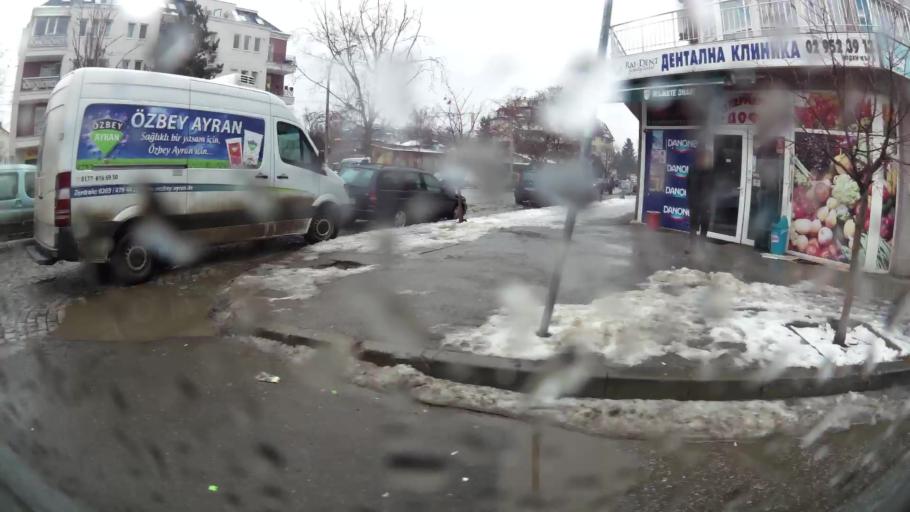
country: BG
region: Sofia-Capital
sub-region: Stolichna Obshtina
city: Sofia
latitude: 42.6757
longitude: 23.2654
